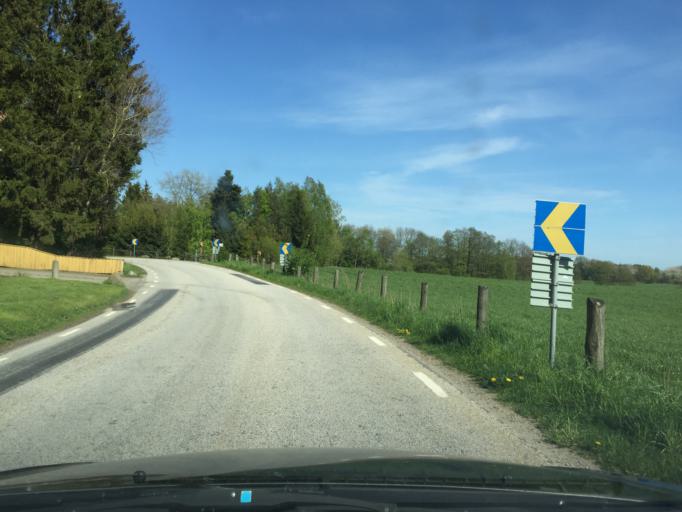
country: SE
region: Skane
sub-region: Sjobo Kommun
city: Blentarp
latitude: 55.5742
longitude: 13.5870
